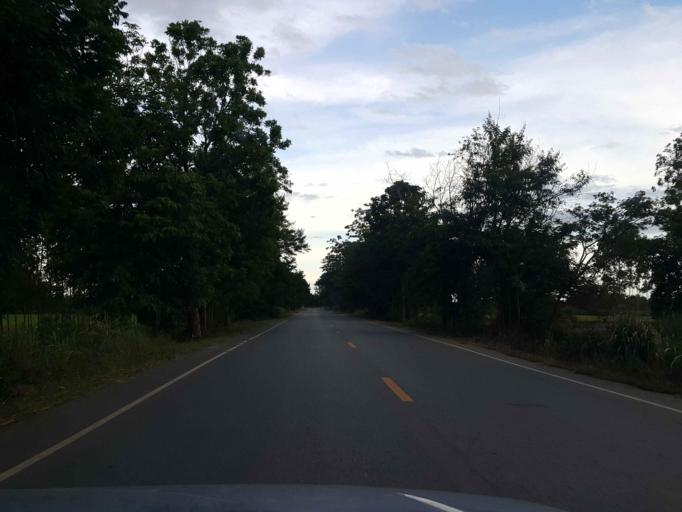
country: TH
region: Sukhothai
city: Sawankhalok
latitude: 17.3761
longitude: 99.7391
